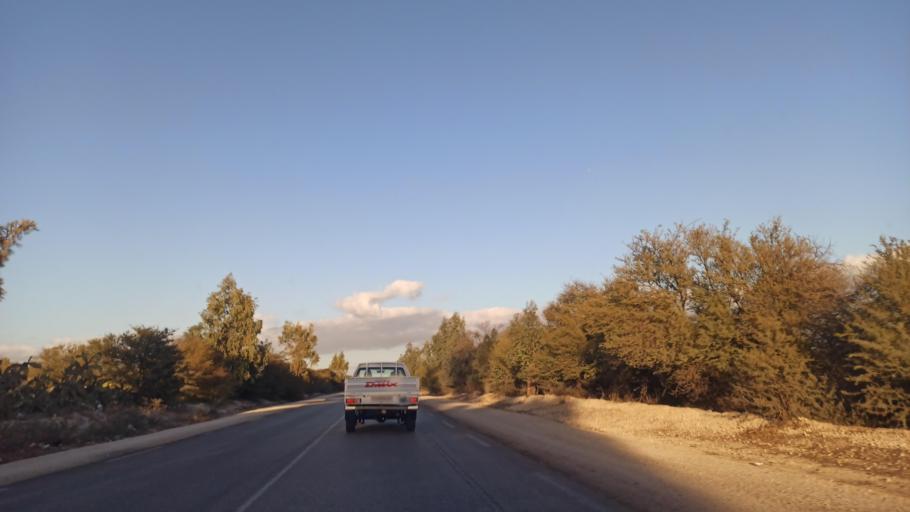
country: TN
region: Al Qayrawan
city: Sbikha
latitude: 35.8560
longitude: 10.2014
